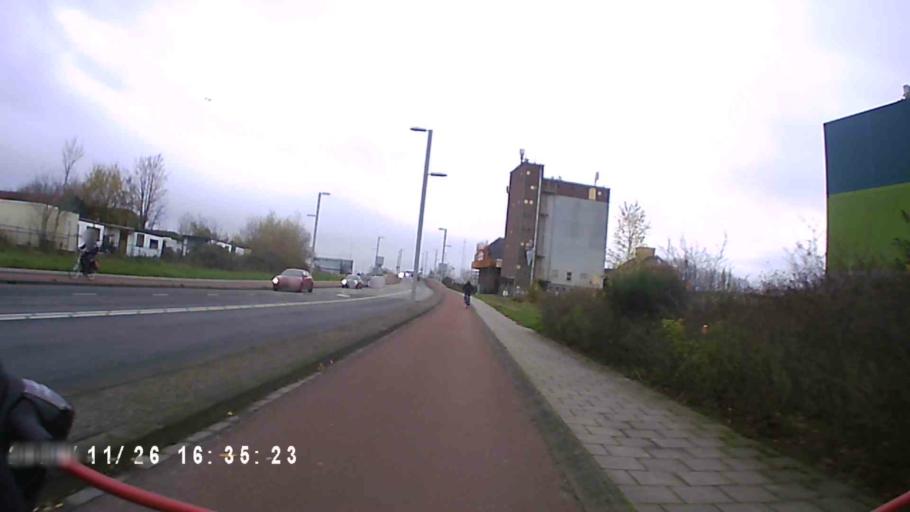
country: NL
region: Groningen
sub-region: Gemeente Groningen
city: Oosterpark
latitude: 53.2218
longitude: 6.5893
